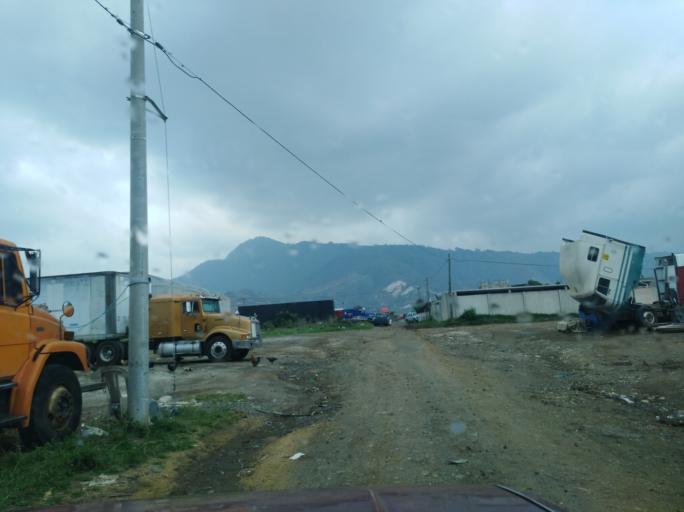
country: GT
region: Guatemala
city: Villa Nueva
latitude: 14.5266
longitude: -90.6230
